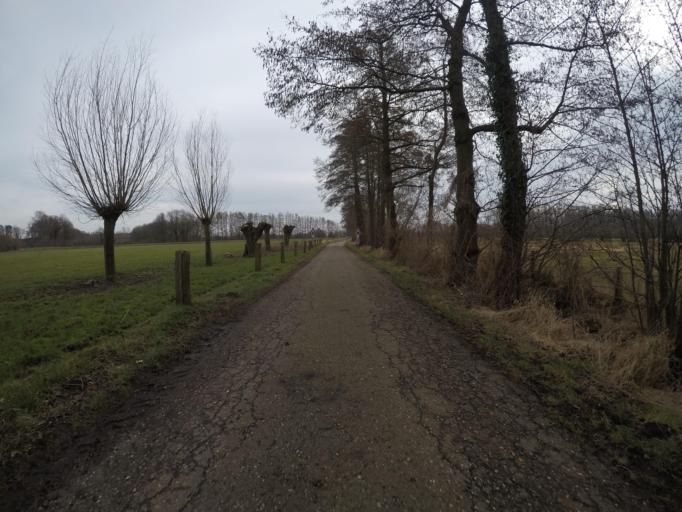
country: DE
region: North Rhine-Westphalia
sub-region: Regierungsbezirk Dusseldorf
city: Hamminkeln
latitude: 51.7525
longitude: 6.6043
